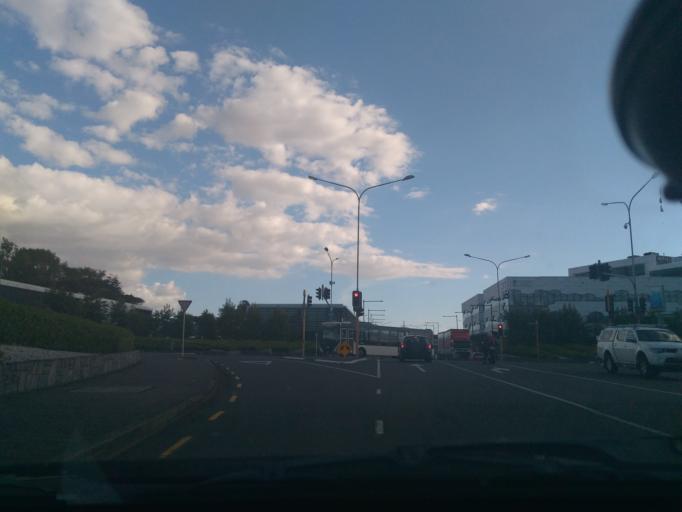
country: NZ
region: Auckland
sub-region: Auckland
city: Tamaki
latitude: -36.9360
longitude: 174.8761
